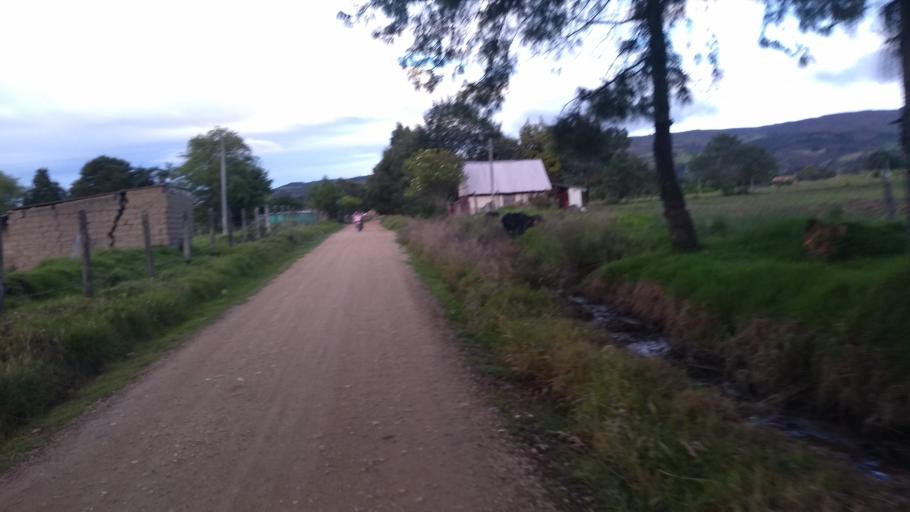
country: CO
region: Boyaca
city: Toca
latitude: 5.6227
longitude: -73.1541
